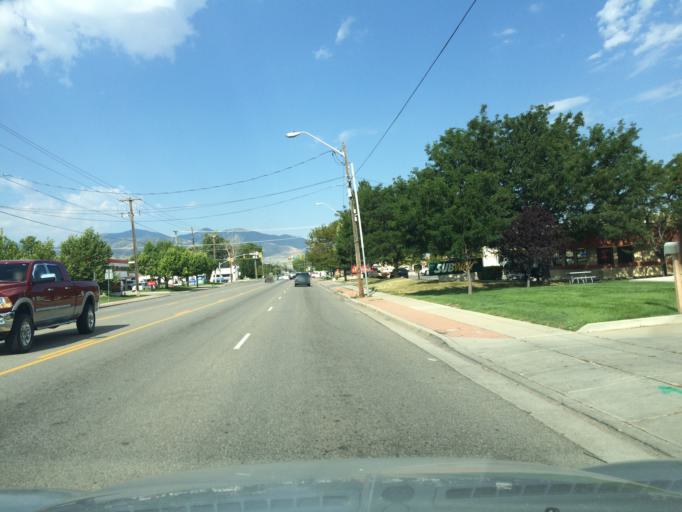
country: US
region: Utah
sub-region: Salt Lake County
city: West Valley City
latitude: 40.6966
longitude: -112.0227
